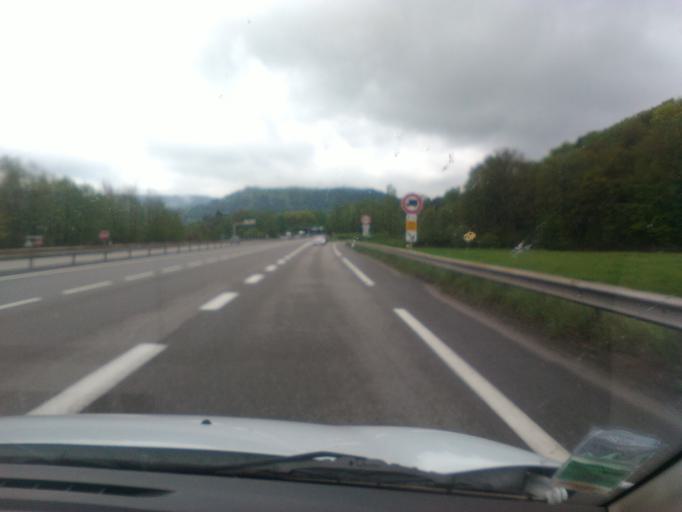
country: FR
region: Lorraine
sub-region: Departement des Vosges
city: Saint-Nabord
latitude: 48.0382
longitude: 6.5821
